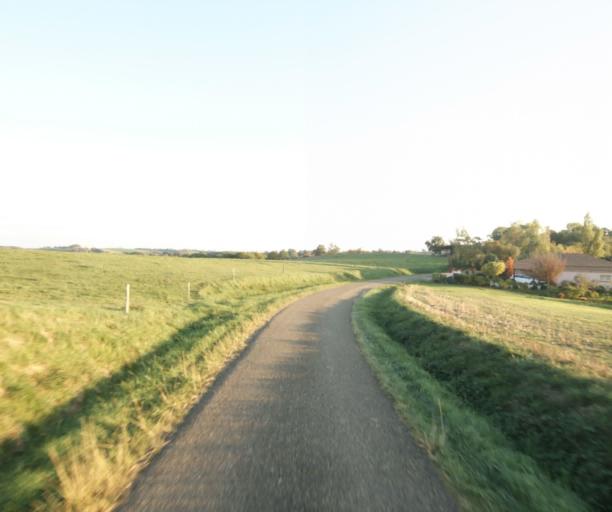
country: FR
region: Midi-Pyrenees
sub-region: Departement du Gers
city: Vic-Fezensac
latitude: 43.7517
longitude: 0.1968
